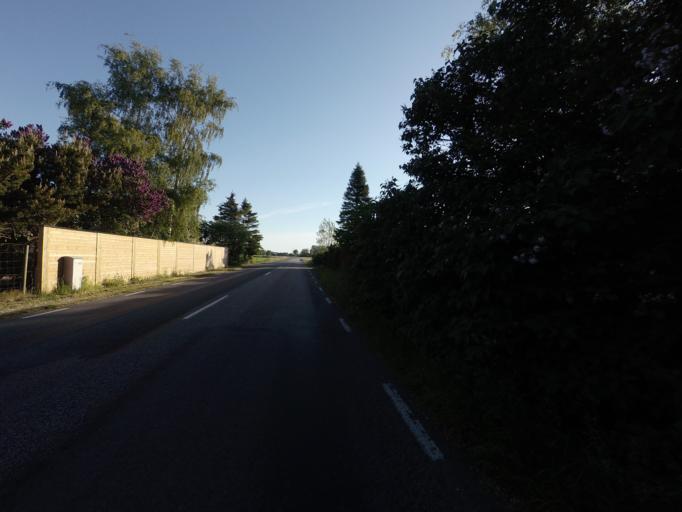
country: SE
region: Skane
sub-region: Hoganas Kommun
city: Hoganas
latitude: 56.2135
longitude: 12.6782
